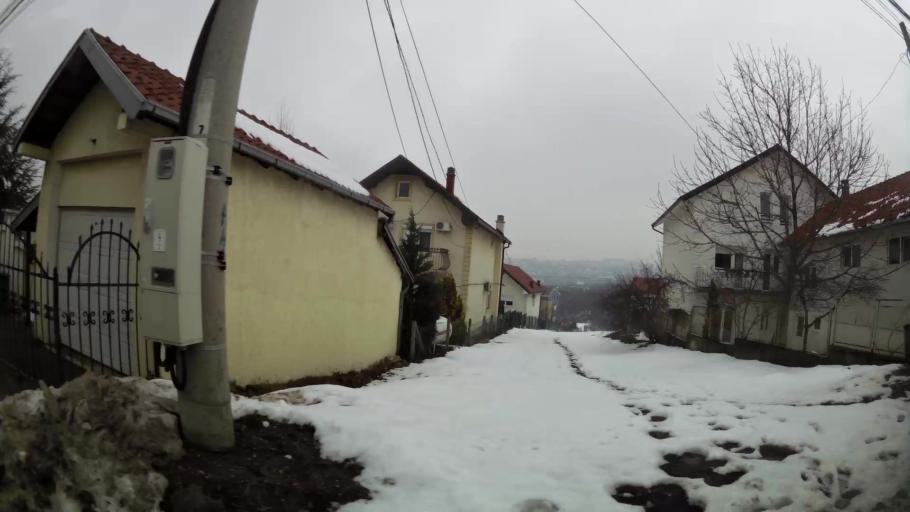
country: RS
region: Central Serbia
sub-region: Belgrade
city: Zvezdara
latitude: 44.7662
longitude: 20.5193
